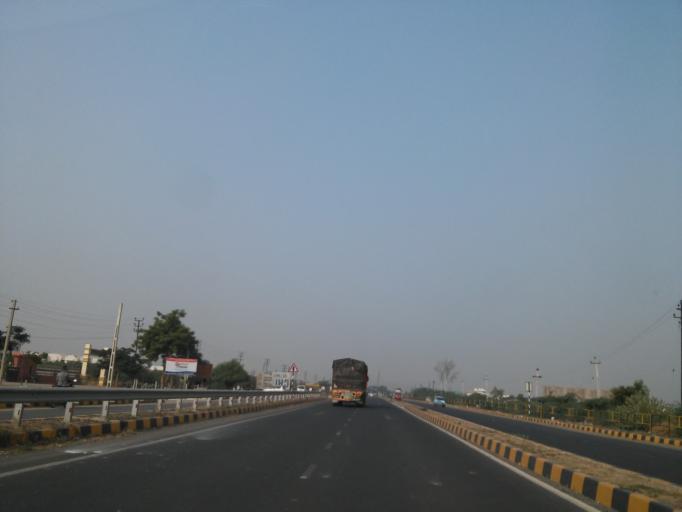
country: IN
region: Gujarat
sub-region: Kachchh
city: Bhuj
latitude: 23.2359
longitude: 69.7297
